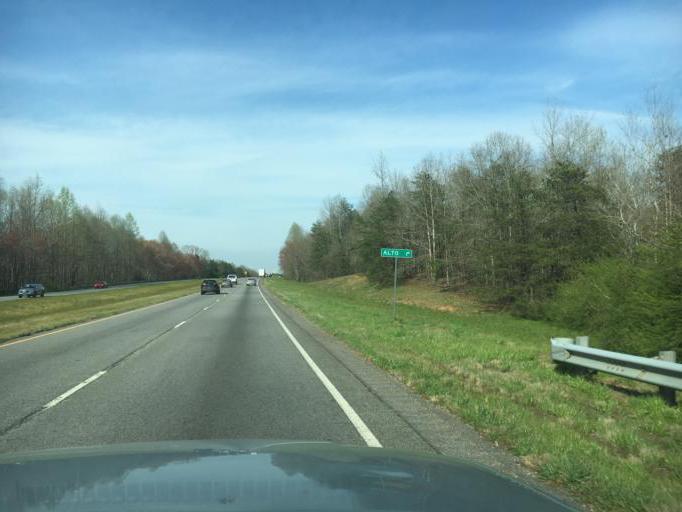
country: US
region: Georgia
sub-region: Habersham County
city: Raoul
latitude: 34.4639
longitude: -83.6034
